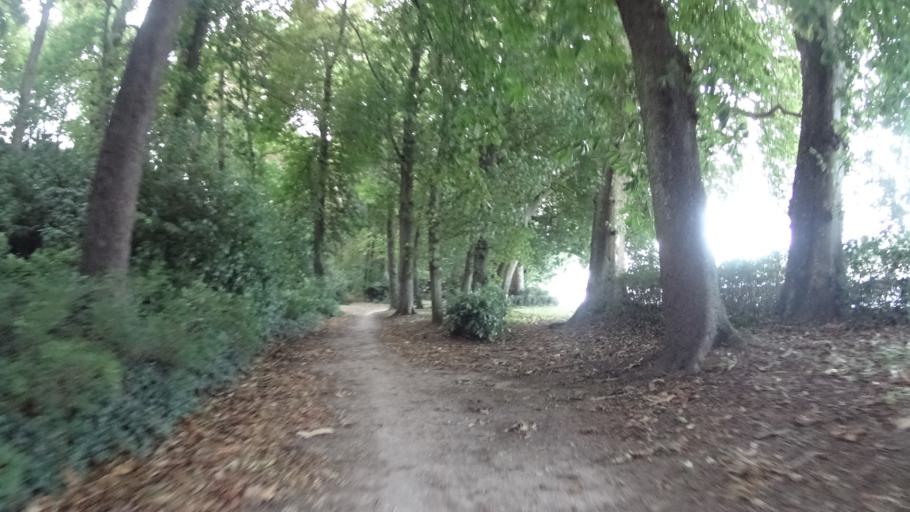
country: FR
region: Centre
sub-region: Departement du Loiret
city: Chateauneuf-sur-Loire
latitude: 47.8594
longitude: 2.2312
